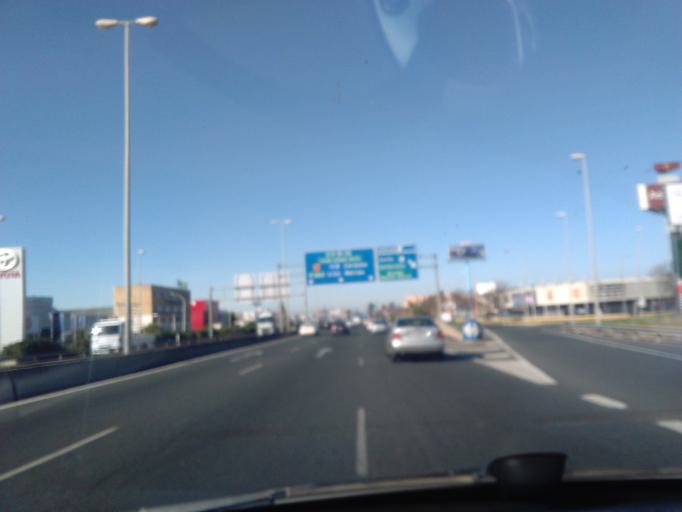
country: ES
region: Andalusia
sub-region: Provincia de Sevilla
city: Sevilla
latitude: 37.3897
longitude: -5.9417
